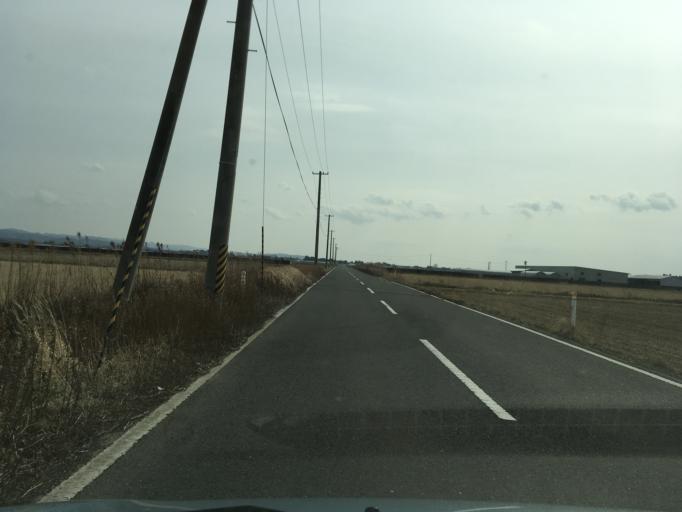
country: JP
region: Iwate
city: Ichinoseki
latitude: 38.7411
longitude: 141.2382
